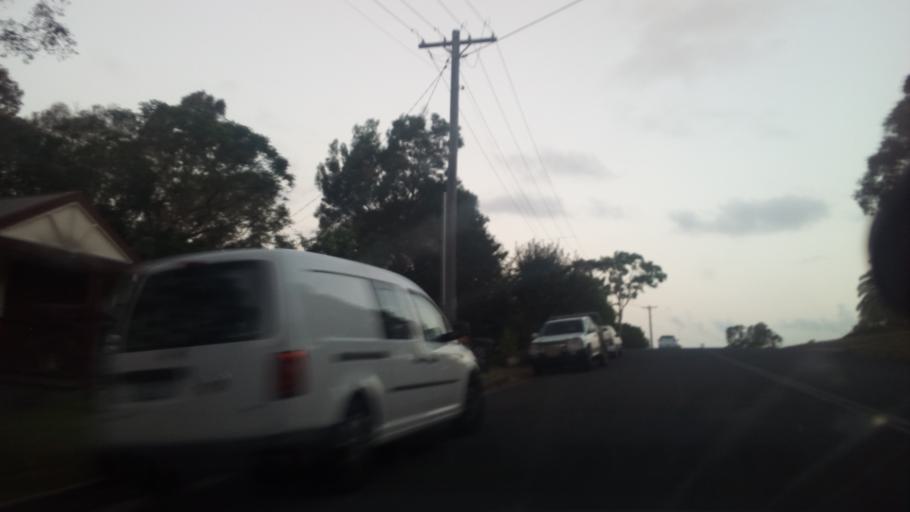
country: AU
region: New South Wales
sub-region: Wollongong
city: Mangerton
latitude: -34.4387
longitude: 150.8758
